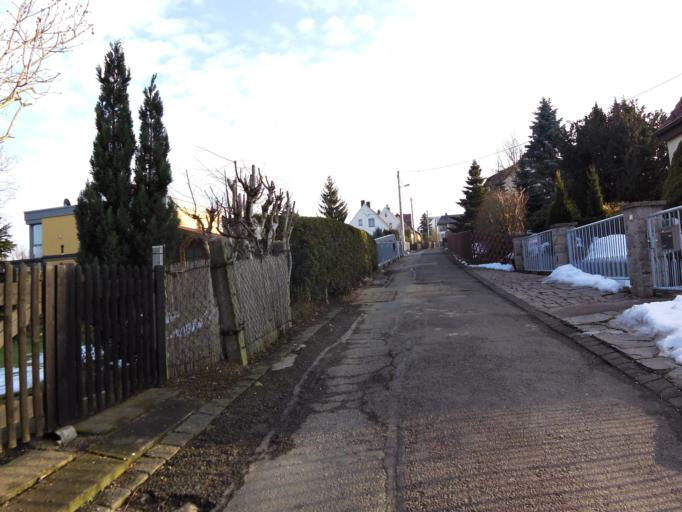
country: DE
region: Saxony
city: Glauchau
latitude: 50.8250
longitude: 12.5559
